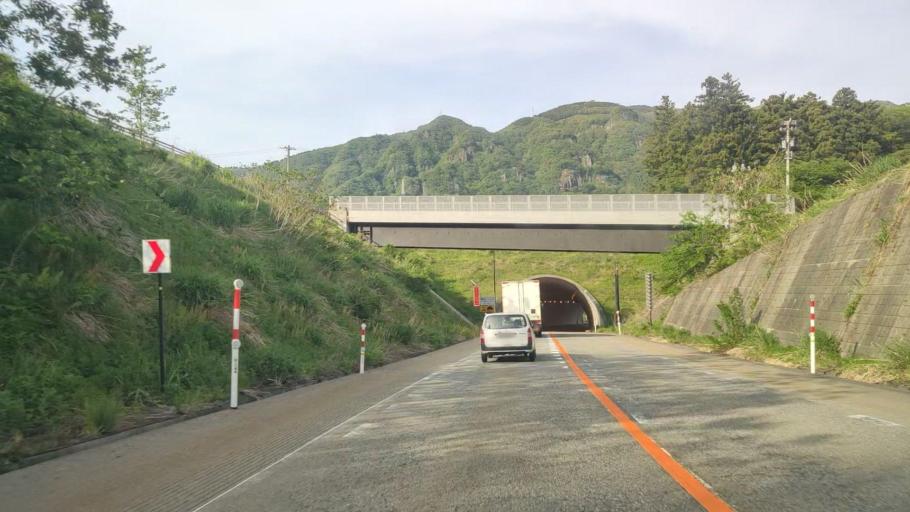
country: JP
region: Toyama
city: Yatsuomachi-higashikumisaka
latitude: 36.5351
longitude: 137.2260
